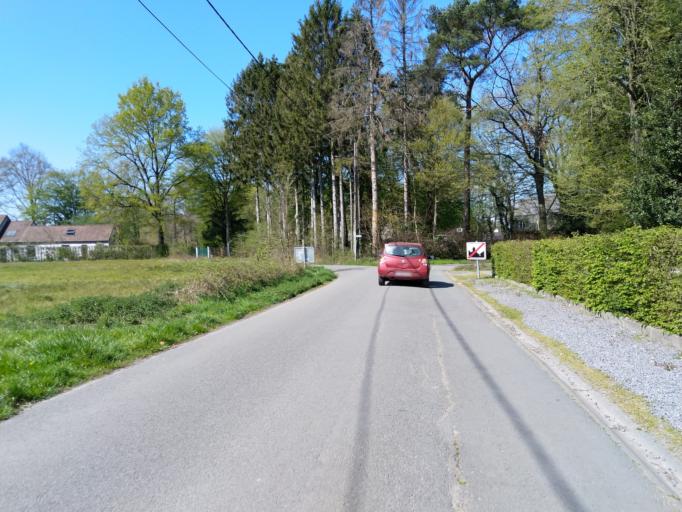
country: BE
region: Wallonia
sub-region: Province du Hainaut
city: Mons
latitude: 50.5037
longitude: 4.0057
